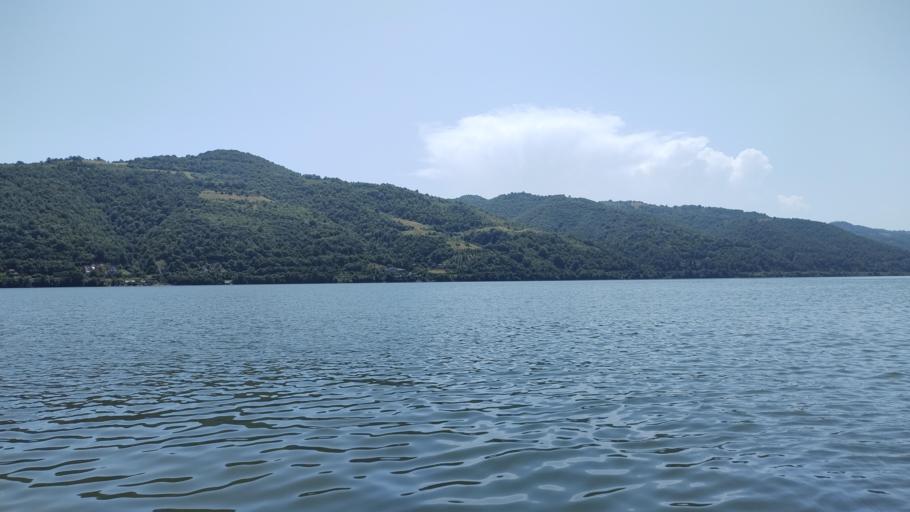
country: RO
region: Mehedinti
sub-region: Comuna Svinita
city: Svinita
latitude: 44.5293
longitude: 22.2068
